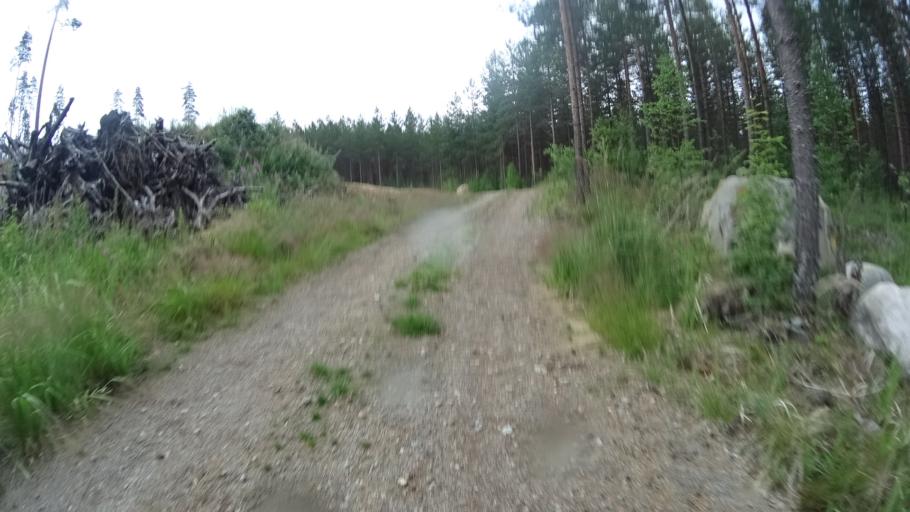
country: FI
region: Uusimaa
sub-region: Helsinki
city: Karkkila
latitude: 60.5959
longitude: 24.1812
